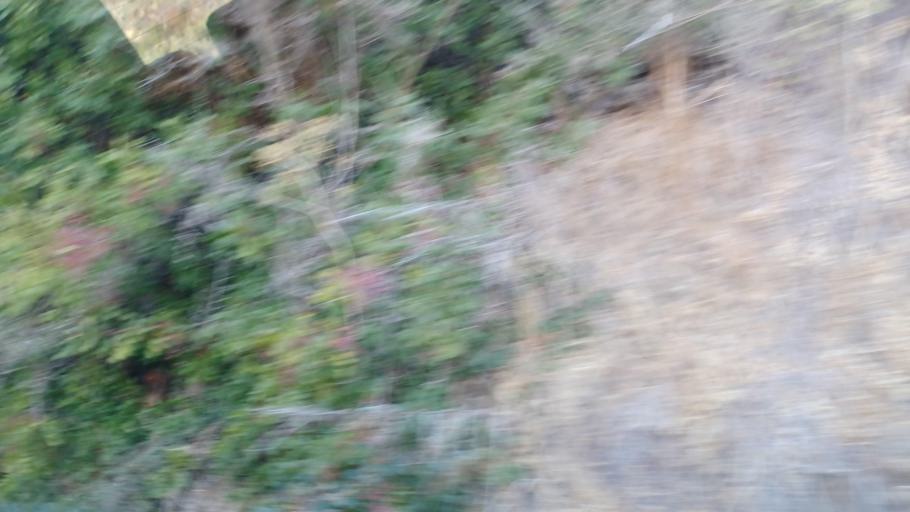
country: CY
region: Pafos
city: Polis
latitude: 34.9823
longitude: 32.4629
